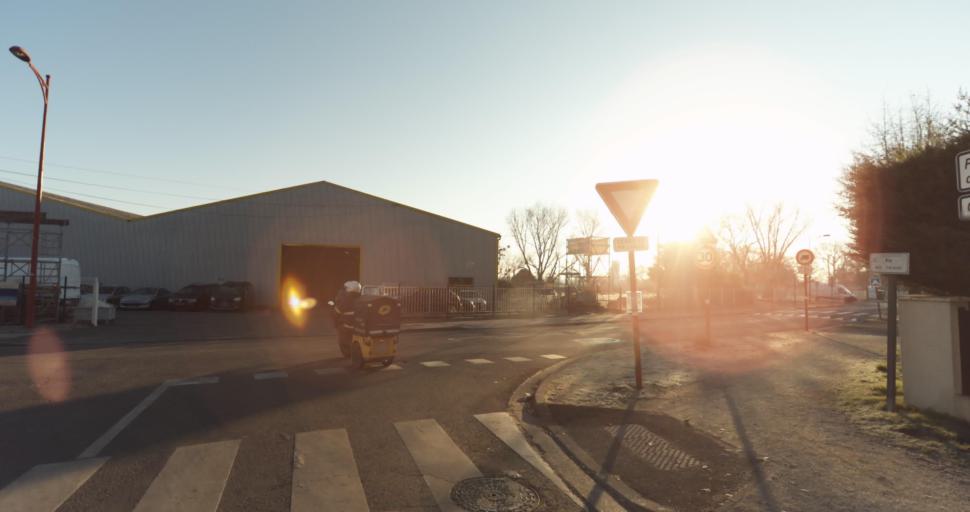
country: FR
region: Aquitaine
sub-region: Departement de la Gironde
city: Carbon-Blanc
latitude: 44.9091
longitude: -0.4960
